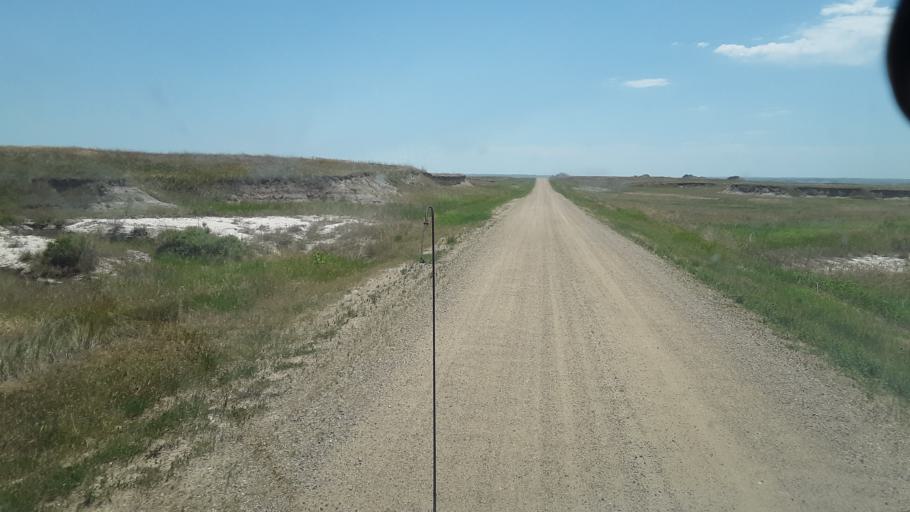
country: US
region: South Dakota
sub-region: Haakon County
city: Philip
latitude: 43.7537
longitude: -101.9995
